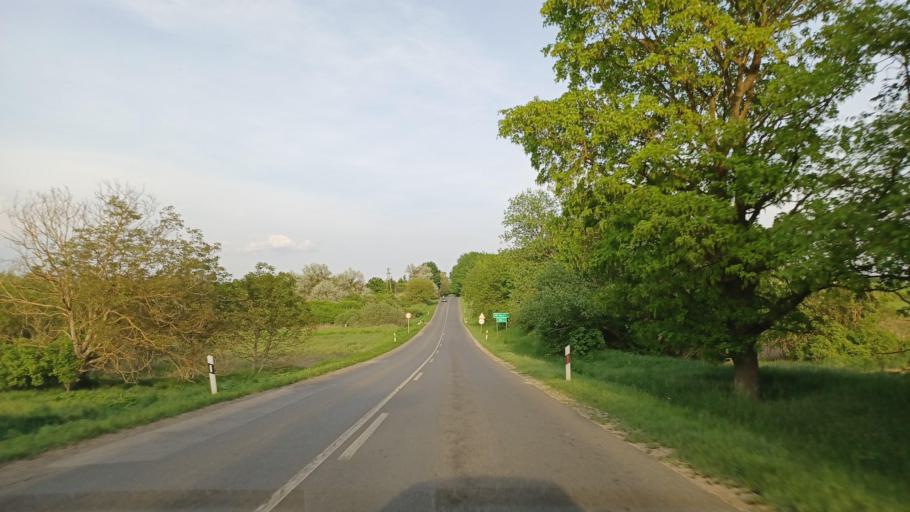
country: HU
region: Baranya
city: Boly
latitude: 45.9881
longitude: 18.5123
